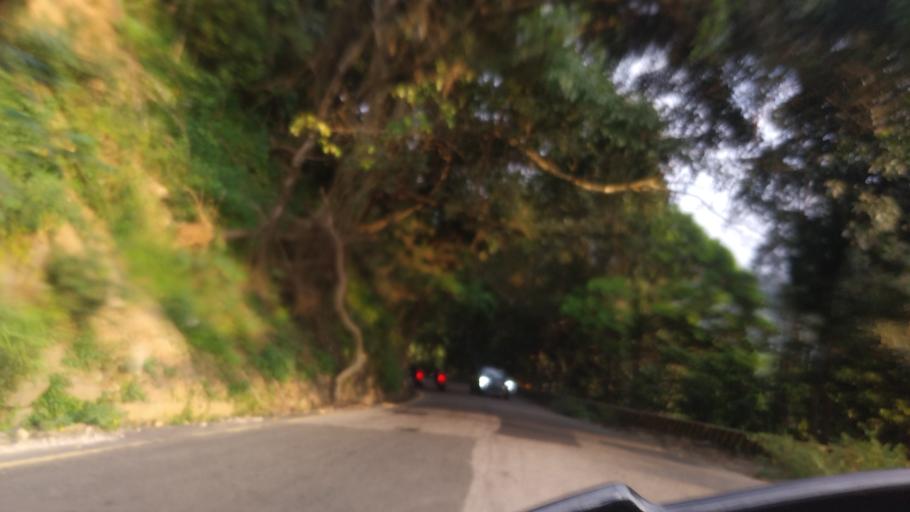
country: IN
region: Kerala
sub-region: Wayanad
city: Kalpetta
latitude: 11.5110
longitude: 76.0213
